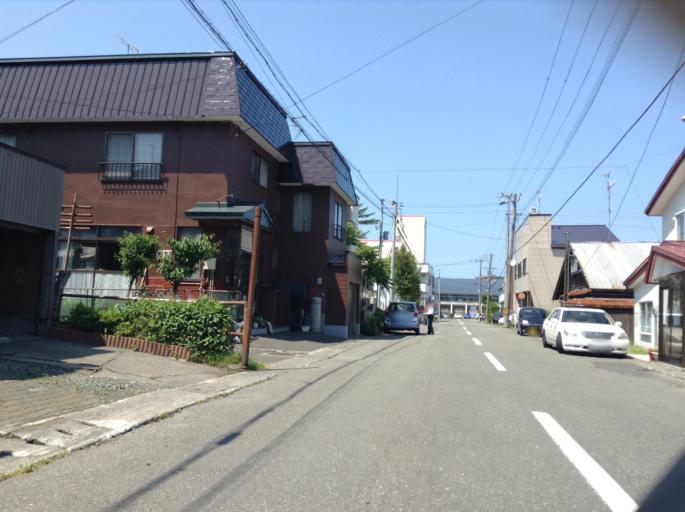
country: JP
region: Hokkaido
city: Wakkanai
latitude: 45.4246
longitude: 141.6704
